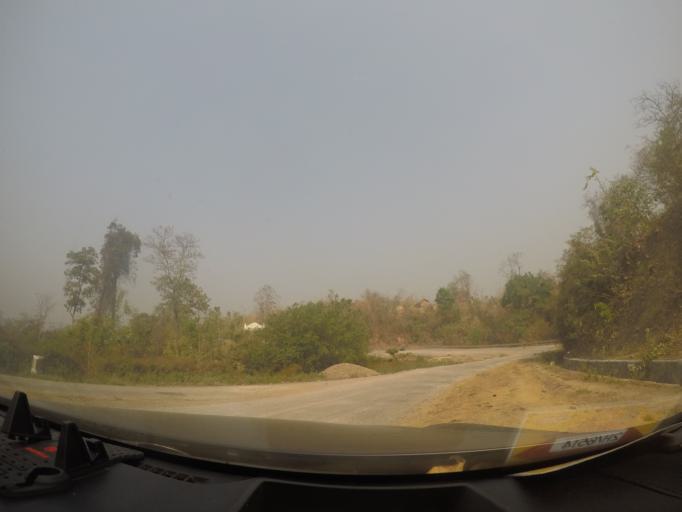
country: MM
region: Magway
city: Taungdwingyi
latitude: 19.9479
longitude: 95.7950
